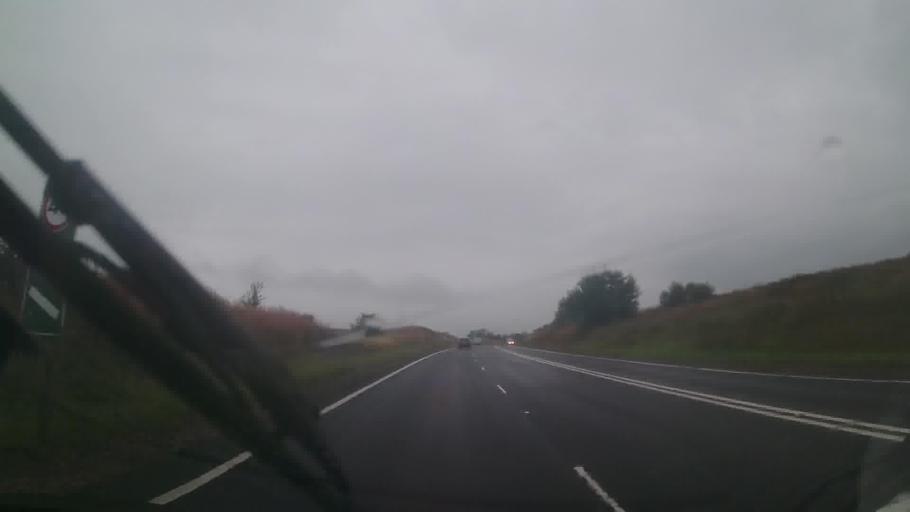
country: GB
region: Scotland
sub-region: North Ayrshire
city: Ardrossan
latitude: 55.6598
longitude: -4.8146
